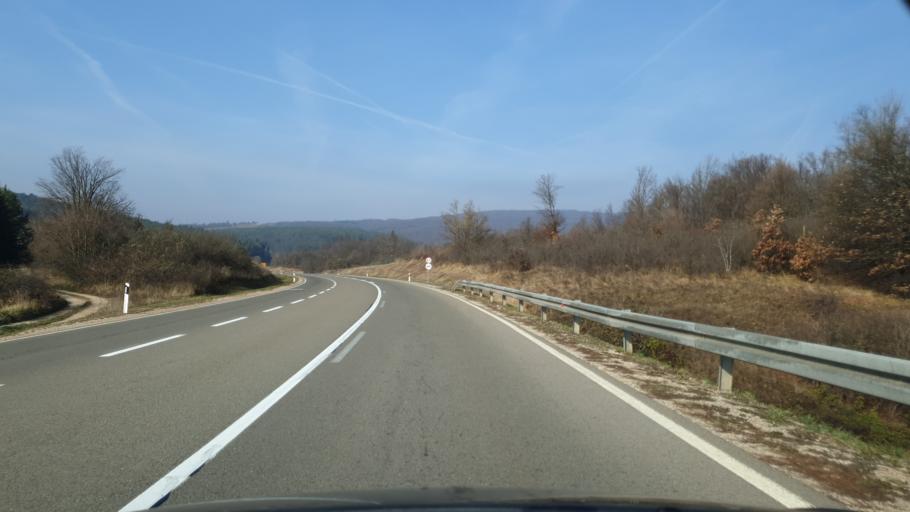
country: RS
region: Central Serbia
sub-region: Nisavski Okrug
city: Razanj
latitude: 43.8390
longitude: 21.7140
